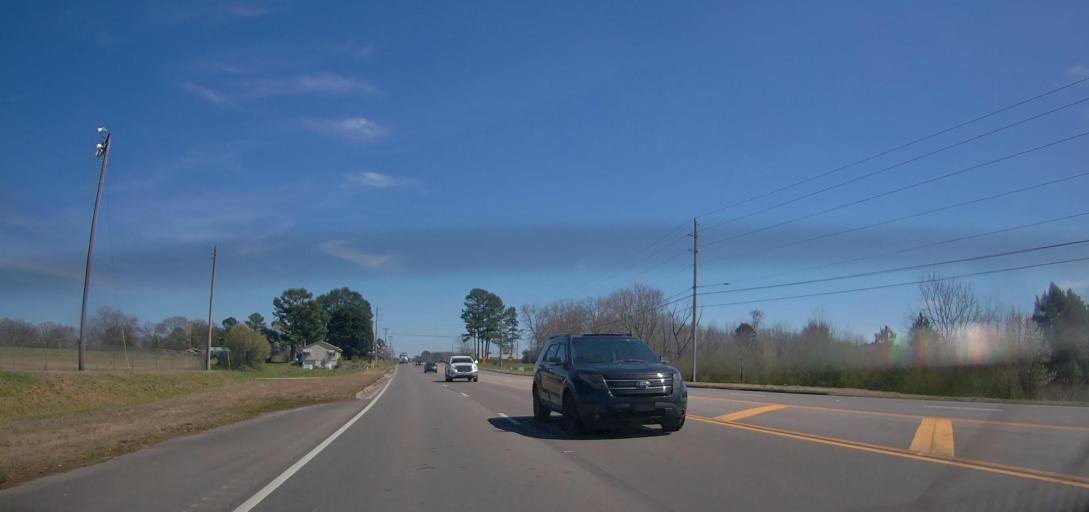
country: US
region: Alabama
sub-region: Cullman County
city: Cullman
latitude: 34.1792
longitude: -86.7476
